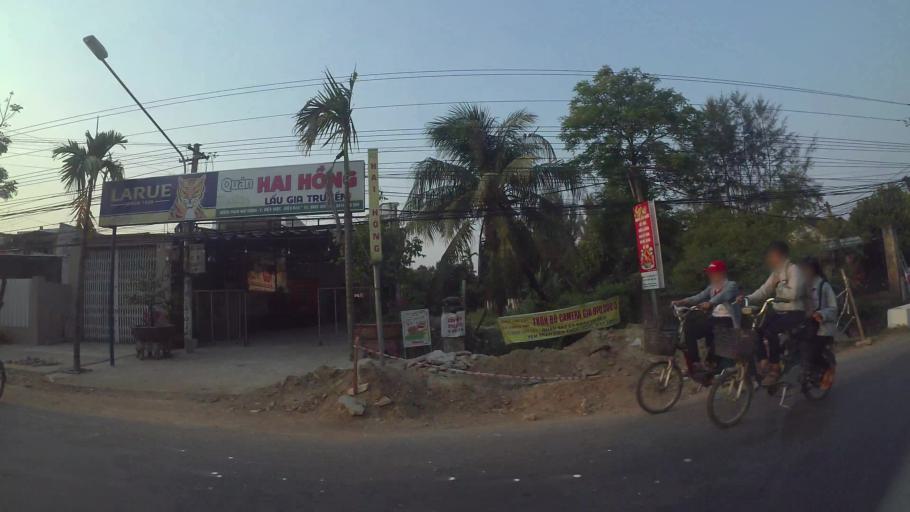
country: VN
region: Da Nang
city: Ngu Hanh Son
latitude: 15.9558
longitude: 108.2505
